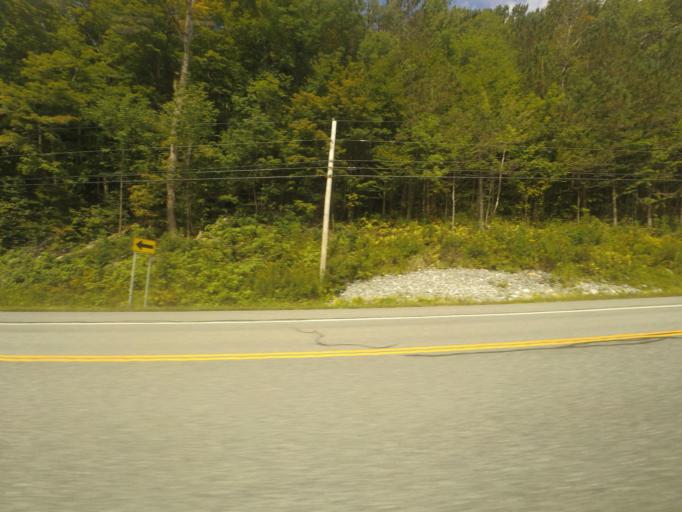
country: US
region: Vermont
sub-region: Bennington County
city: Bennington
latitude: 42.8796
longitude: -73.0995
